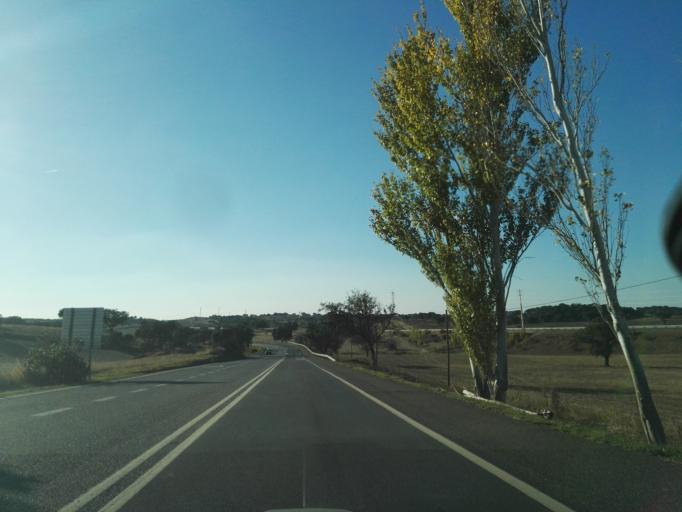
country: PT
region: Evora
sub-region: Vila Vicosa
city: Vila Vicosa
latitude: 38.8476
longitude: -7.3645
